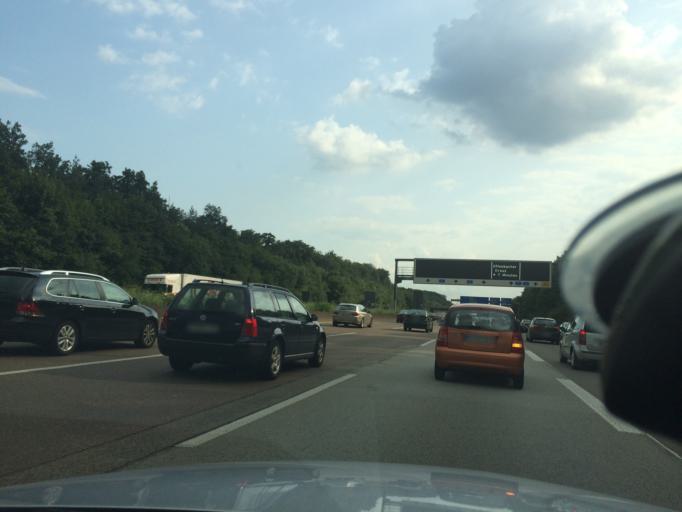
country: DE
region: Hesse
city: Niederrad
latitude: 50.0705
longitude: 8.6127
